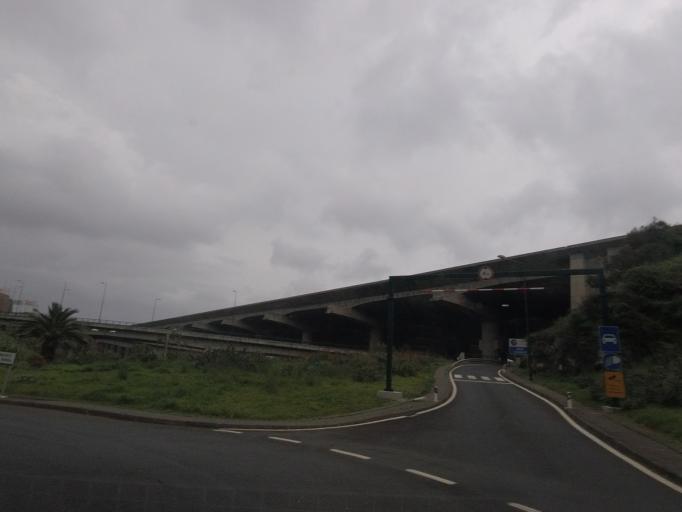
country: PT
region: Madeira
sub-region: Machico
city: Machico
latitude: 32.7017
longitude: -16.7722
